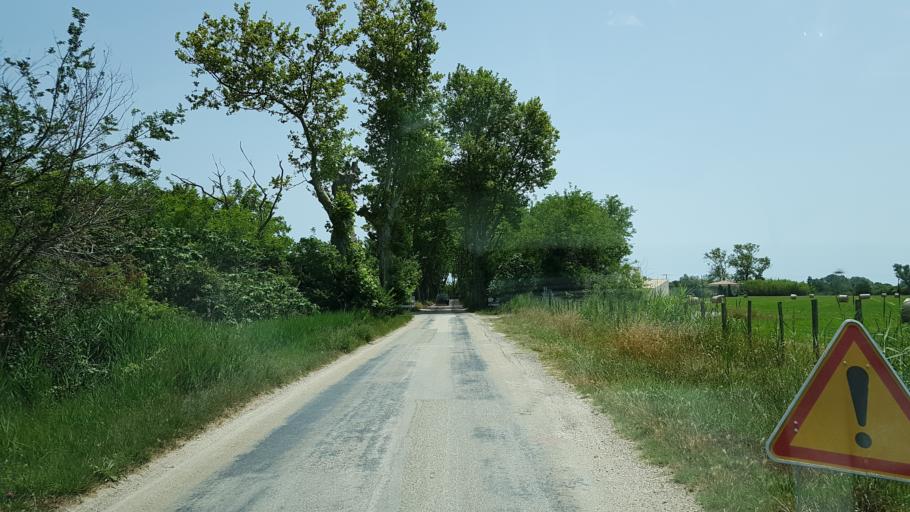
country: FR
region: Provence-Alpes-Cote d'Azur
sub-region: Departement des Bouches-du-Rhone
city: Port-Saint-Louis-du-Rhone
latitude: 43.4495
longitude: 4.6605
